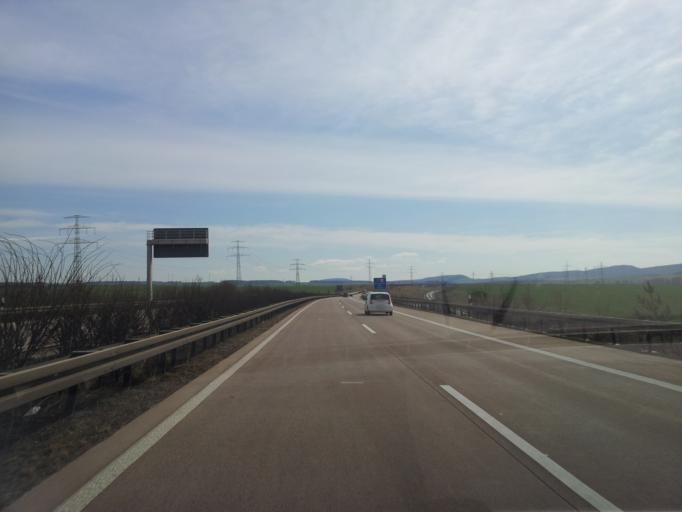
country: DE
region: Thuringia
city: Alkersleben
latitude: 50.8517
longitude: 11.0092
